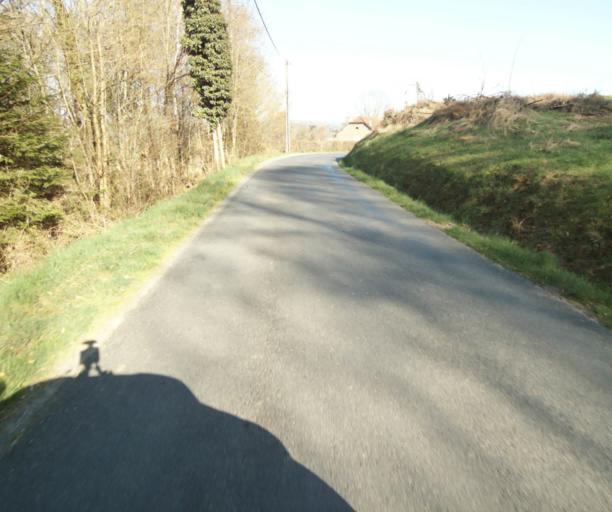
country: FR
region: Limousin
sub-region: Departement de la Correze
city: Saint-Clement
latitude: 45.2949
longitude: 1.6984
